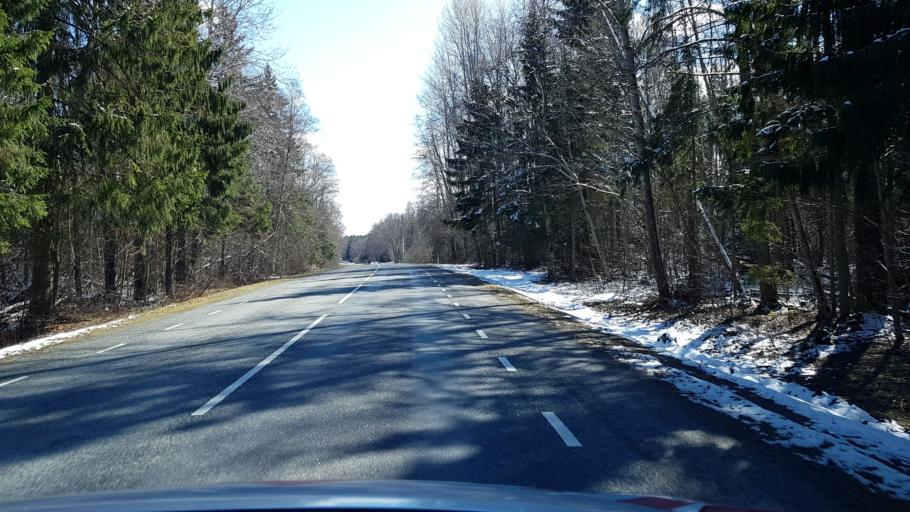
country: EE
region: Laeaene-Virumaa
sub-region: Tapa vald
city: Tapa
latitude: 59.4371
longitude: 25.9612
